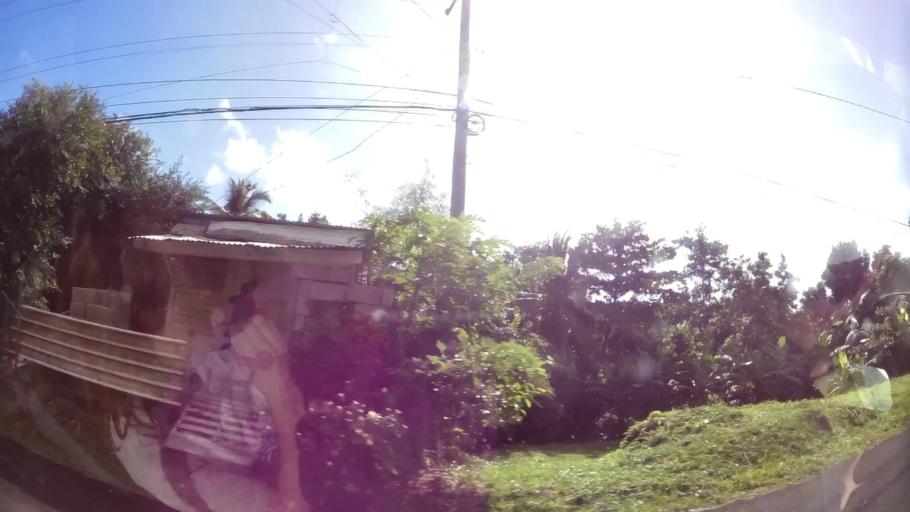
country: DM
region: Saint Andrew
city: Marigot
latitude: 15.5113
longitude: -61.2631
